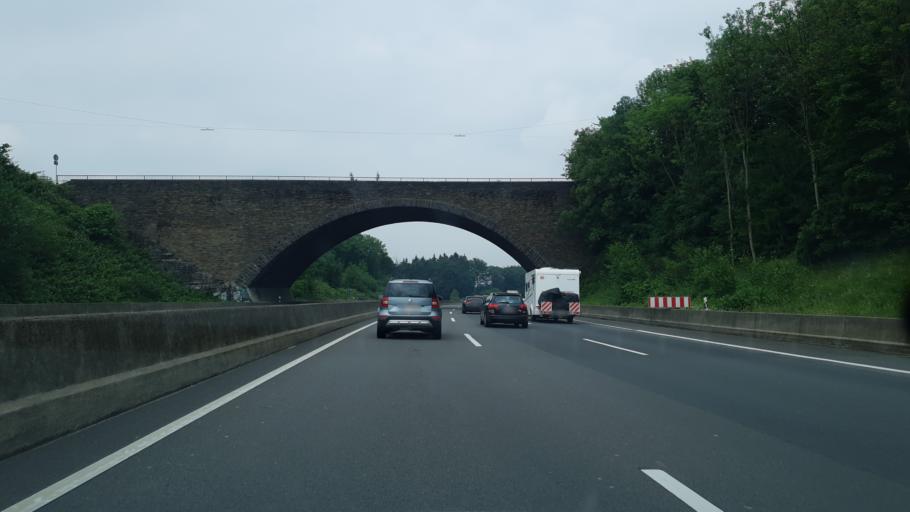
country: DE
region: North Rhine-Westphalia
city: Wermelskirchen
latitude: 51.1373
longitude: 7.1904
